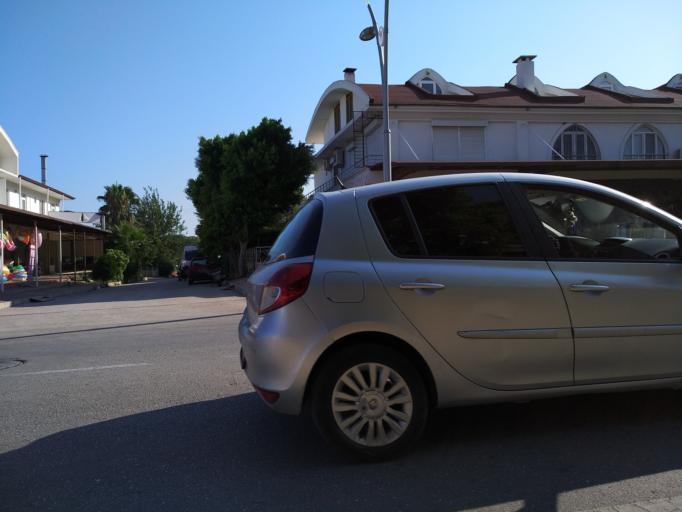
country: TR
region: Antalya
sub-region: Kemer
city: Goeynuek
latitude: 36.6651
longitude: 30.5553
